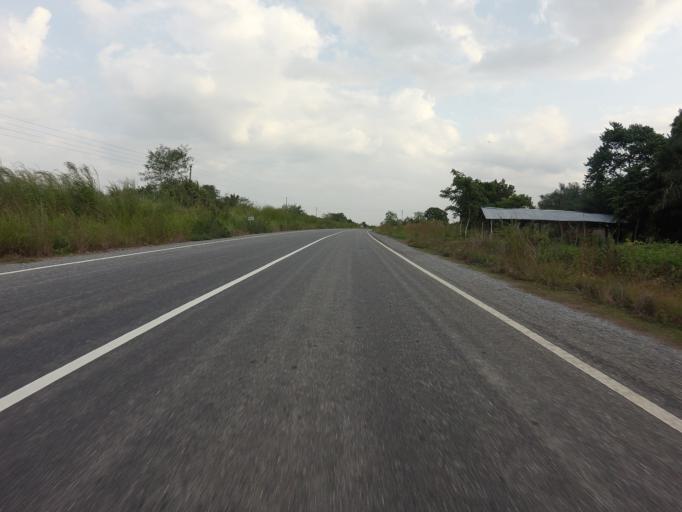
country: GH
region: Volta
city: Ho
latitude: 6.3524
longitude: 0.5375
